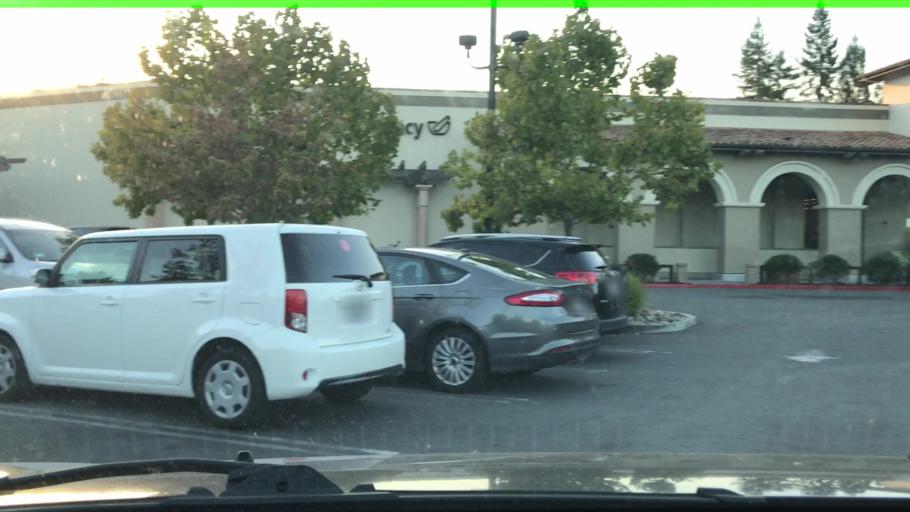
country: US
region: California
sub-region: San Mateo County
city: Menlo Park
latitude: 37.4501
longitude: -122.1785
